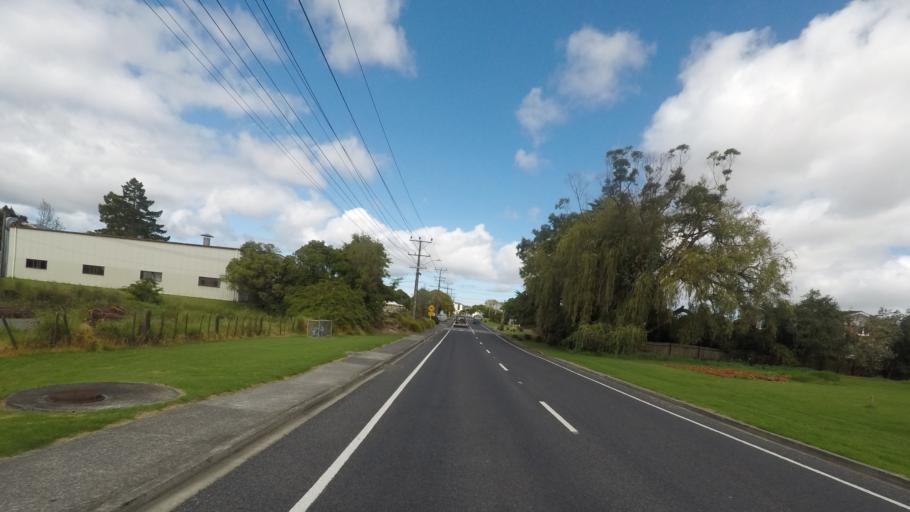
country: NZ
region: Auckland
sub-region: Auckland
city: Muriwai Beach
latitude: -36.7705
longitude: 174.5486
